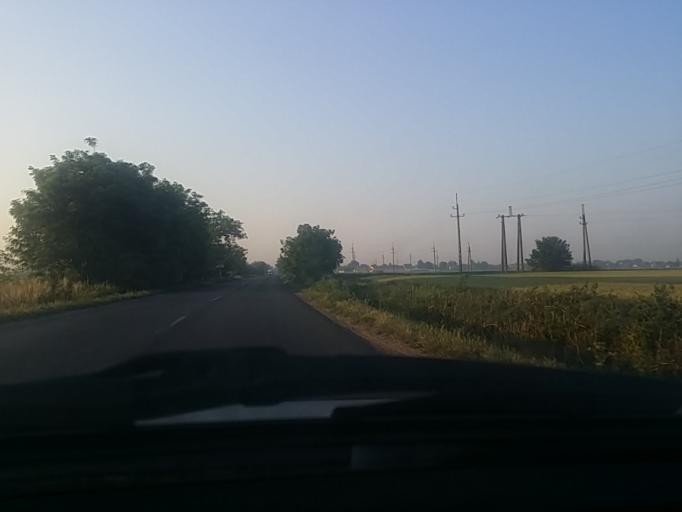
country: HU
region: Pest
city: Nagykata
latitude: 47.4323
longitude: 19.7308
